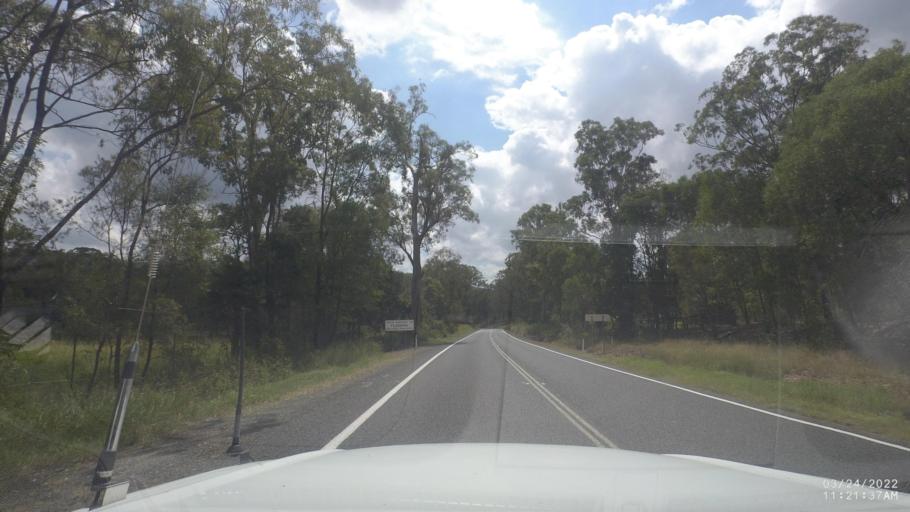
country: AU
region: Queensland
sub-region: Logan
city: Windaroo
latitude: -27.7996
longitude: 153.1769
